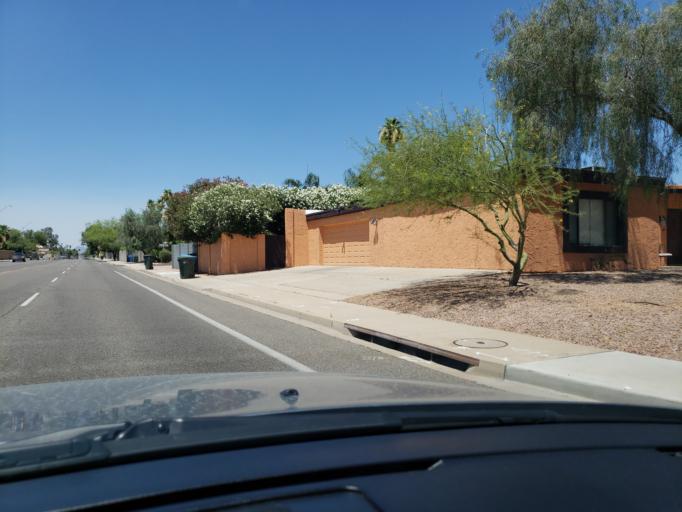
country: US
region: Arizona
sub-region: Maricopa County
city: Paradise Valley
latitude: 33.6070
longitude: -111.9433
